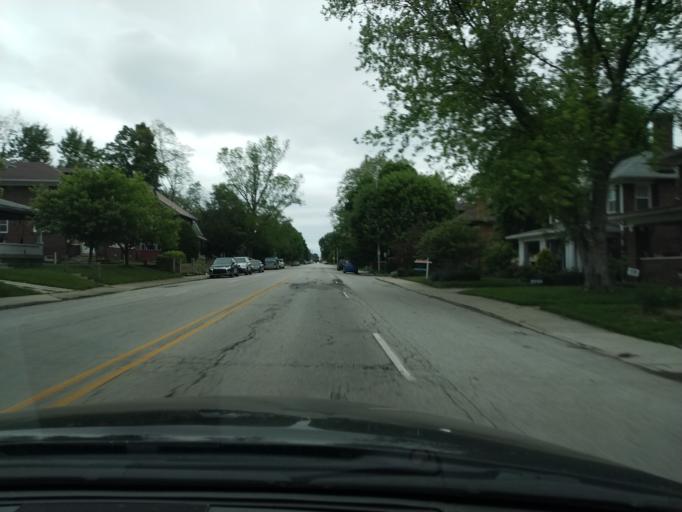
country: US
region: Indiana
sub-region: Marion County
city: Broad Ripple
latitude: 39.8240
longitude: -86.1498
